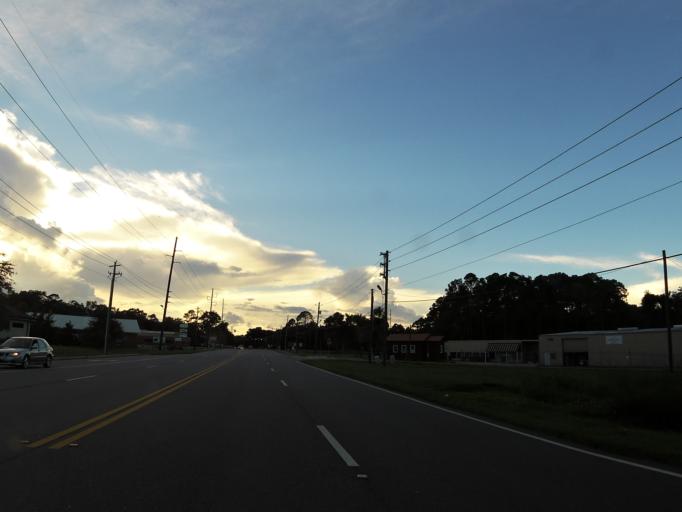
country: US
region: Georgia
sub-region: Camden County
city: St. Marys
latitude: 30.7415
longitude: -81.5519
